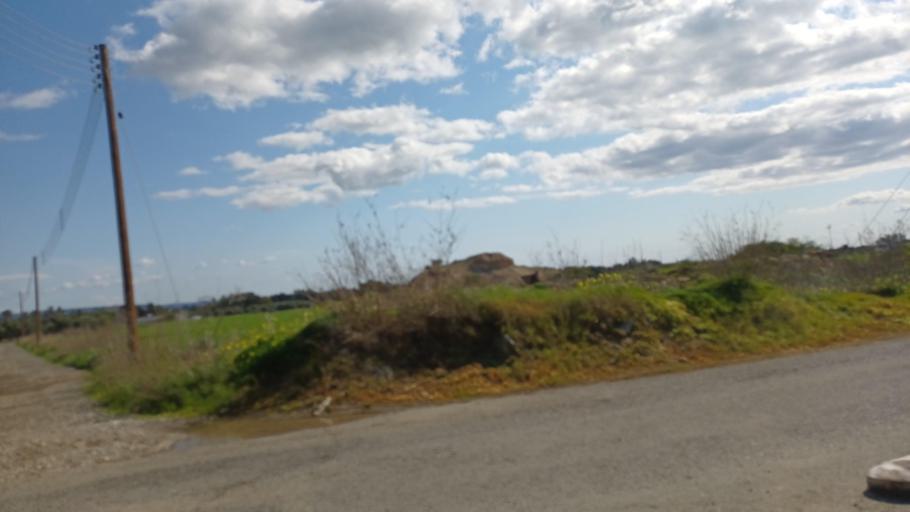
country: CY
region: Pafos
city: Paphos
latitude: 34.7514
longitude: 32.4378
